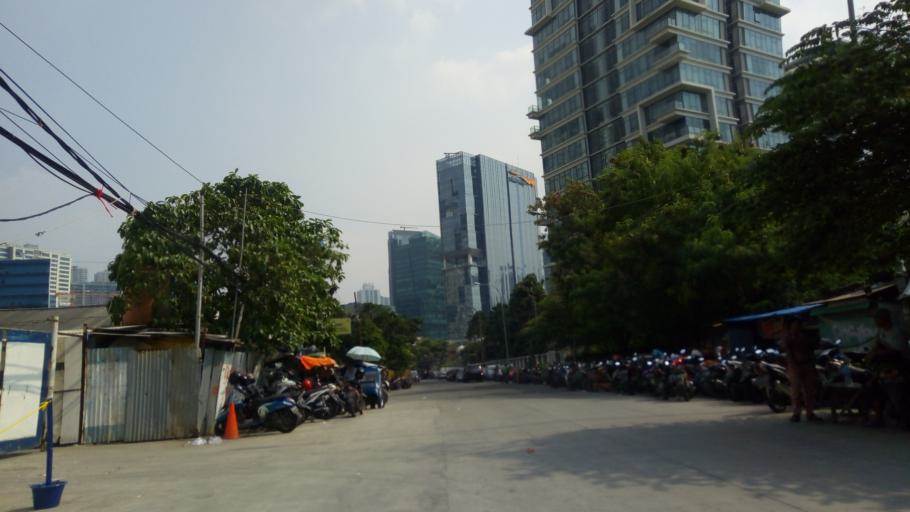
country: ID
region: Jakarta Raya
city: Jakarta
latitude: -6.2138
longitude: 106.8340
